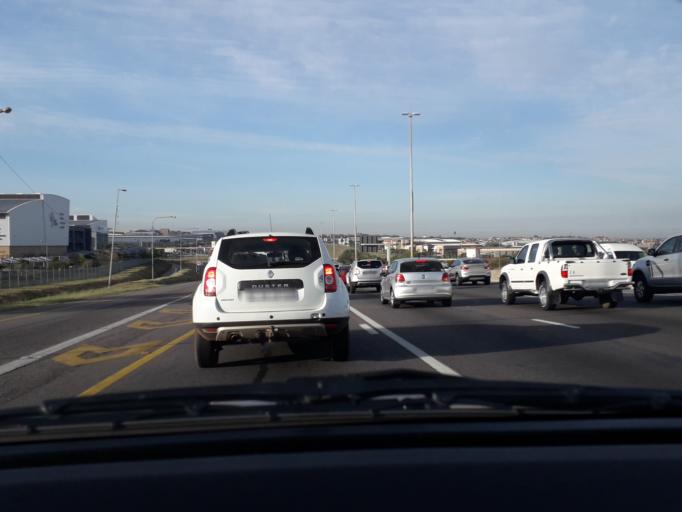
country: ZA
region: Gauteng
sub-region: City of Johannesburg Metropolitan Municipality
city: Midrand
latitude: -25.9237
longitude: 28.1482
